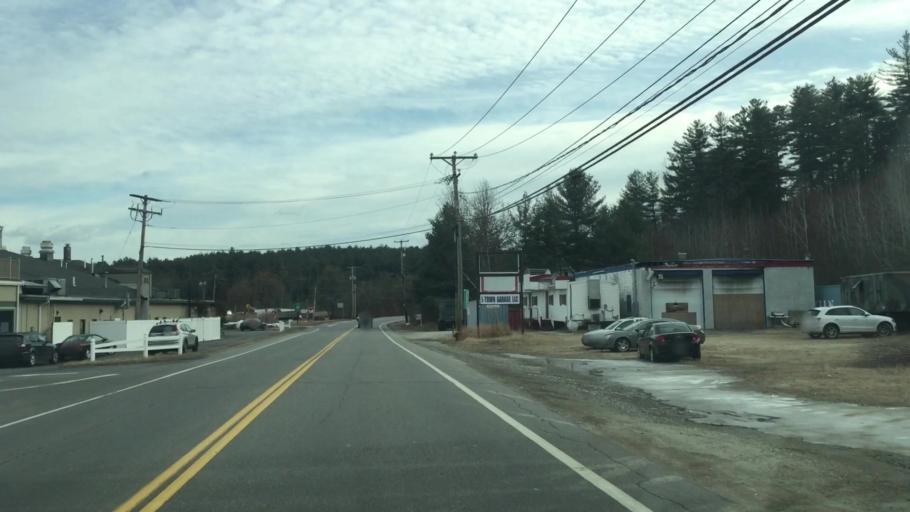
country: US
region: New Hampshire
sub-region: Hillsborough County
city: Manchester
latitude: 42.9354
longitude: -71.4143
